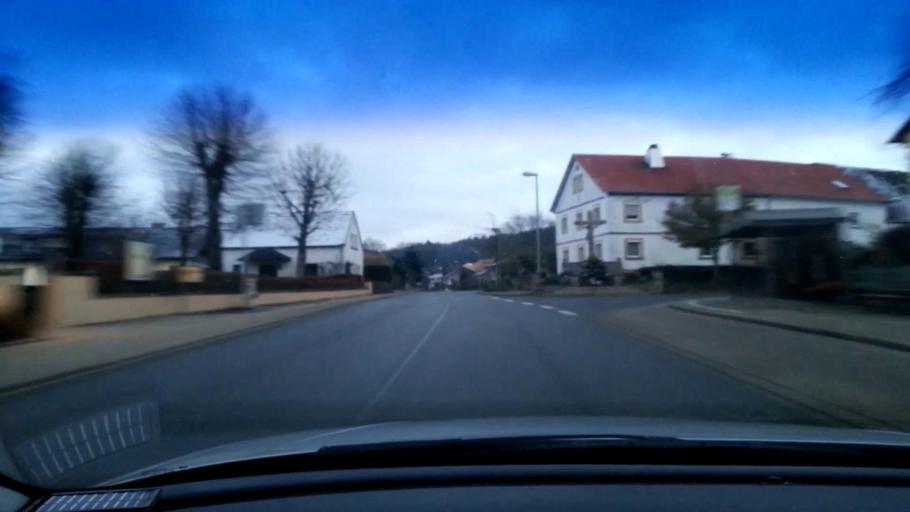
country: DE
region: Bavaria
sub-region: Upper Franconia
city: Pettstadt
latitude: 49.8463
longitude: 10.8953
